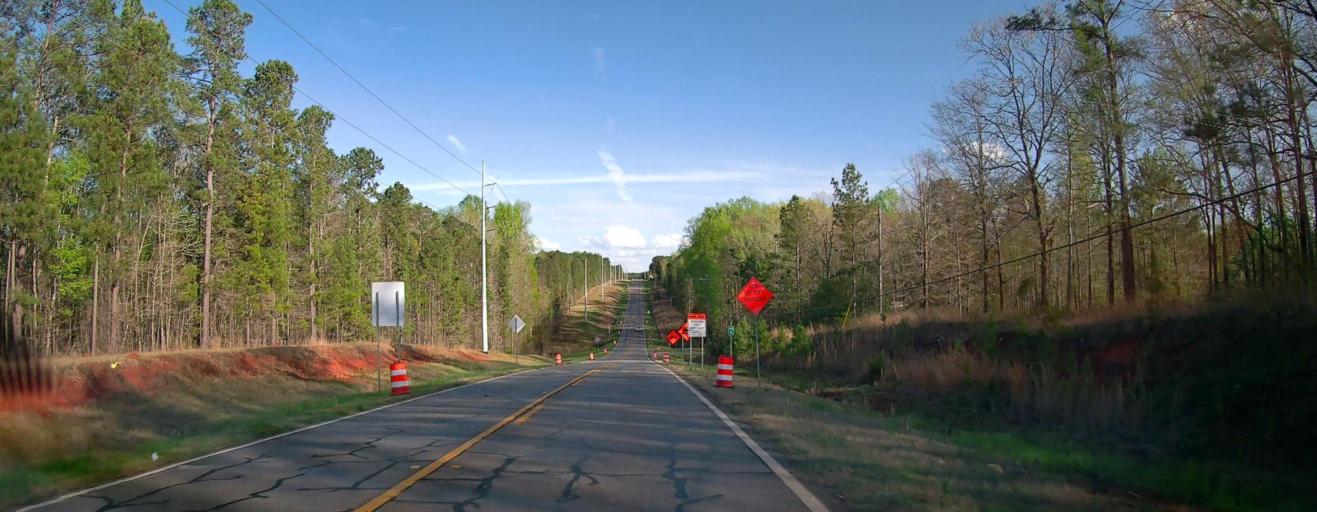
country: US
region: Georgia
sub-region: Baldwin County
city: Milledgeville
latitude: 33.1363
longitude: -83.3263
